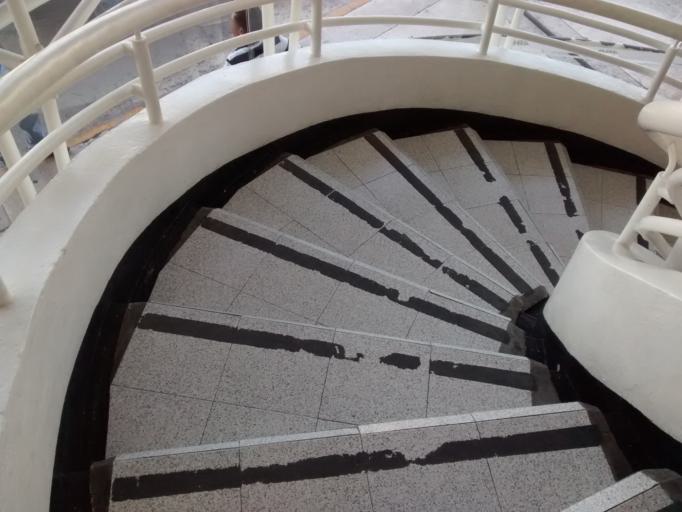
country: MX
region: Quintana Roo
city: Cancun
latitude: 21.1647
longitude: -86.8266
